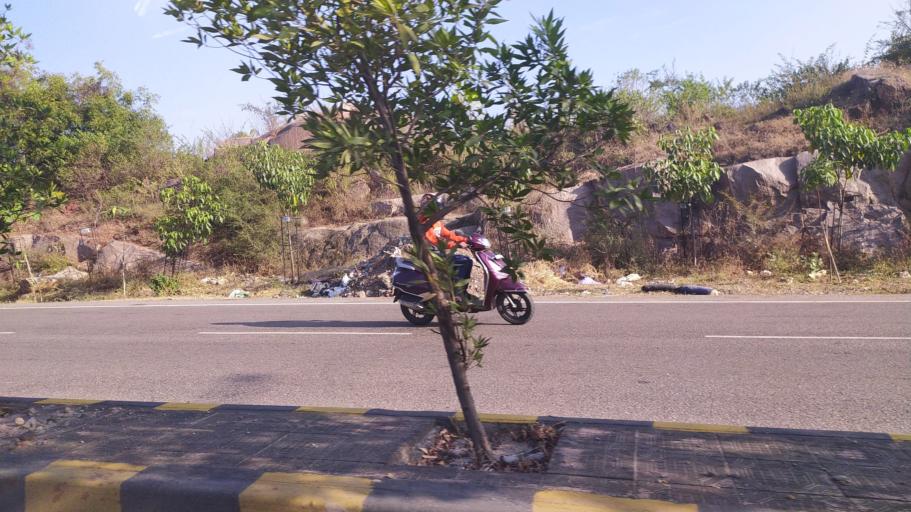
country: IN
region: Telangana
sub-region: Hyderabad
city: Hyderabad
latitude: 17.3210
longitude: 78.3863
